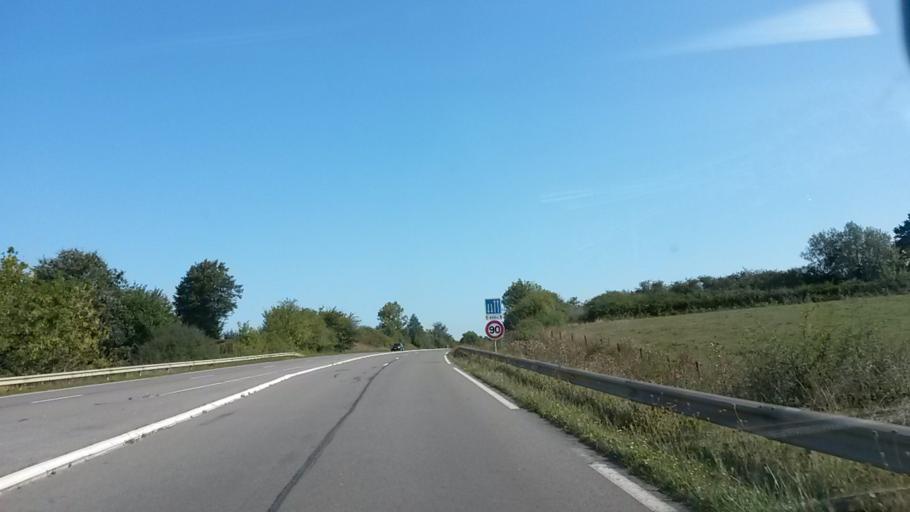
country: FR
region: Picardie
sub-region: Departement de l'Aisne
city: La Flamengrie
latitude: 50.0510
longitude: 3.9282
